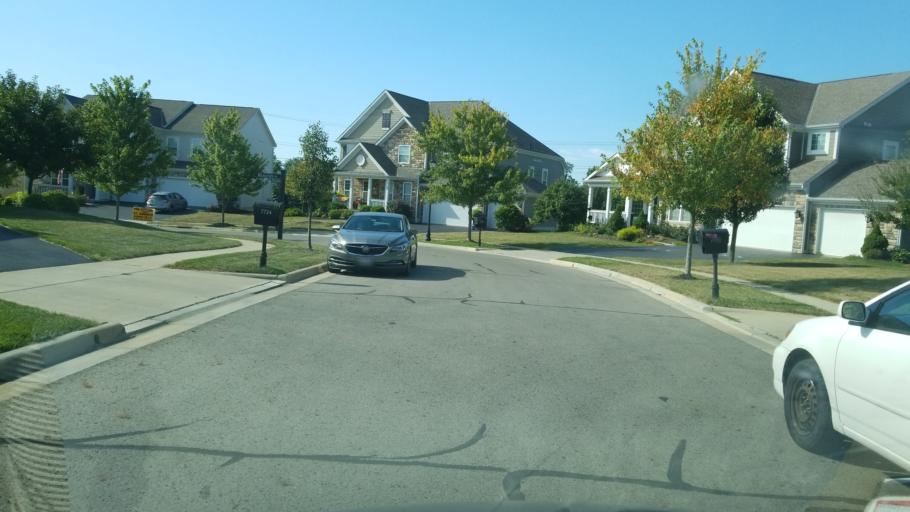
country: US
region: Ohio
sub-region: Franklin County
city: Worthington
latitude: 40.1176
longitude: -83.0480
